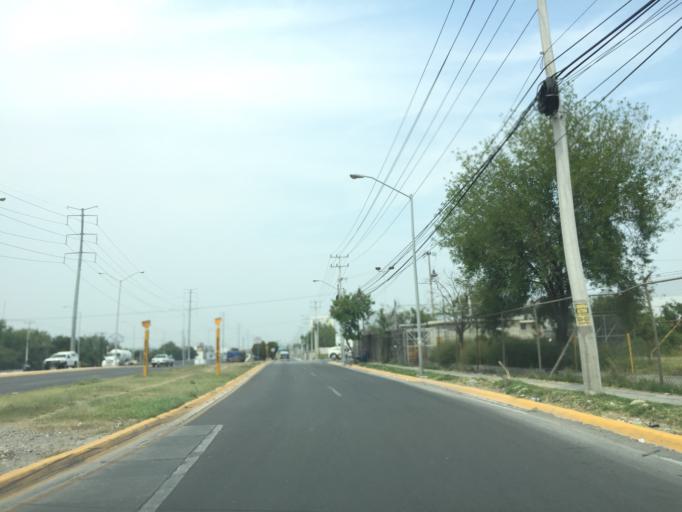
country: MX
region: Nuevo Leon
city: Apodaca
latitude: 25.7656
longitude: -100.2014
